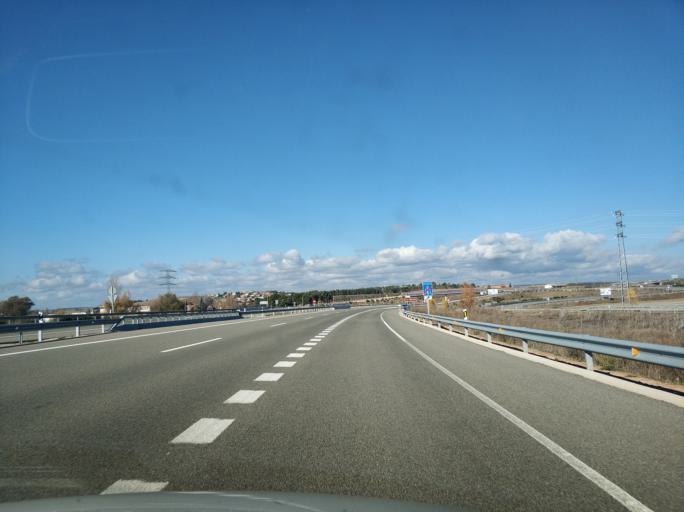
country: ES
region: Castille and Leon
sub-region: Provincia de Soria
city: Almazan
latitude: 41.4665
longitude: -2.5239
